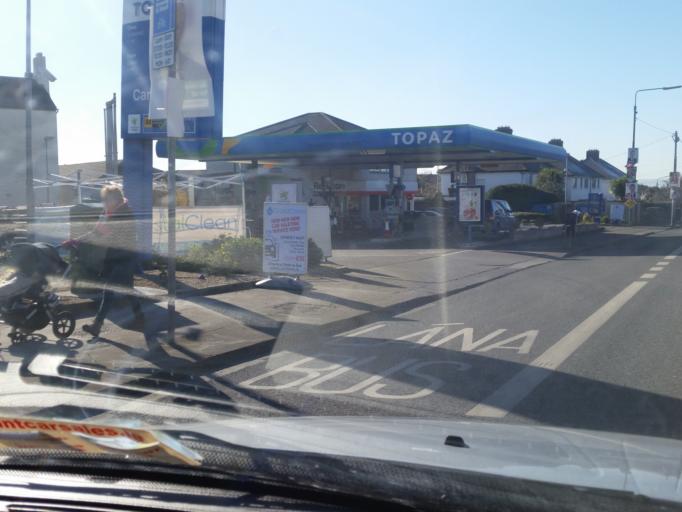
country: IE
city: Killester
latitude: 53.3738
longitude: -6.2001
